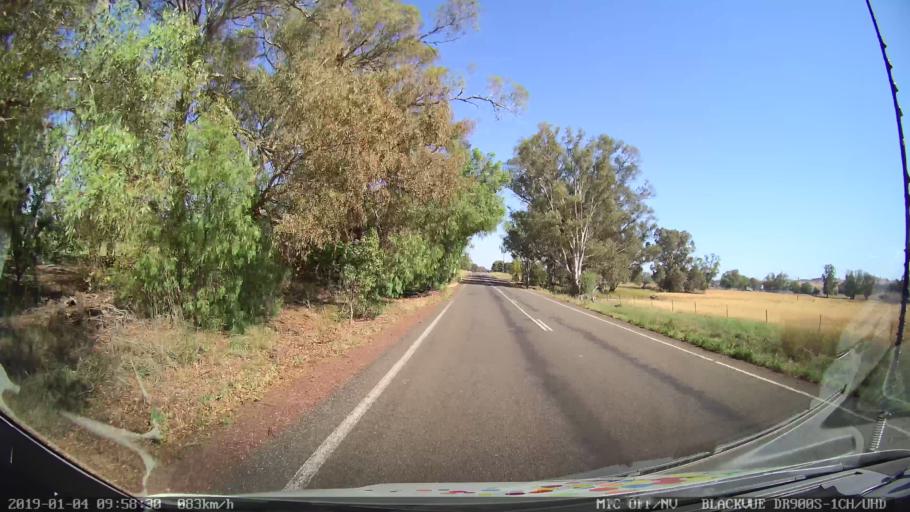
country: AU
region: New South Wales
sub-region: Cabonne
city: Canowindra
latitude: -33.5179
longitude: 148.3939
